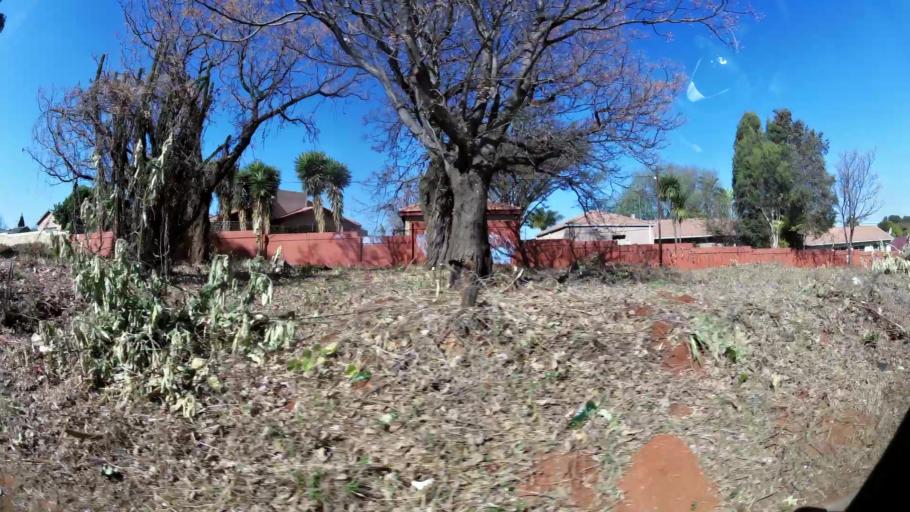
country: ZA
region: Gauteng
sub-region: City of Johannesburg Metropolitan Municipality
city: Roodepoort
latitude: -26.1268
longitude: 27.9194
